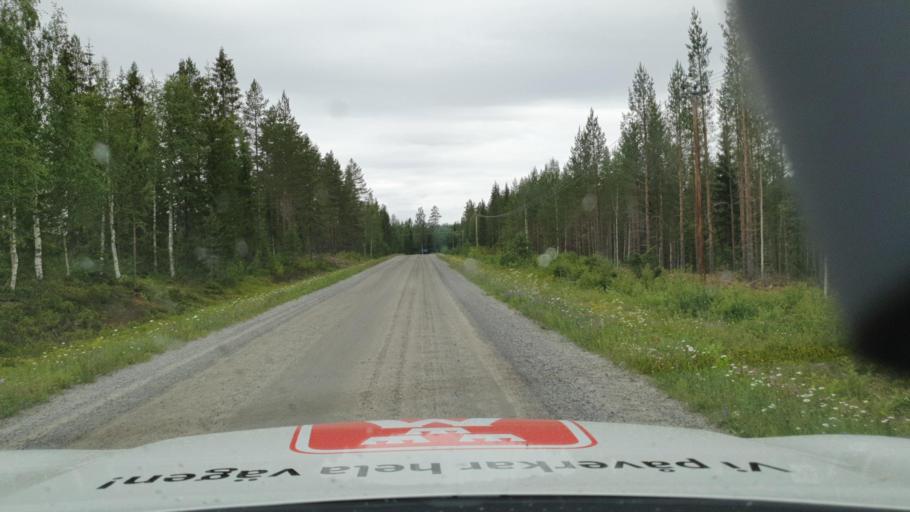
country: SE
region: Vaesterbotten
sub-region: Nordmalings Kommun
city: Nordmaling
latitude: 63.7638
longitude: 19.4797
